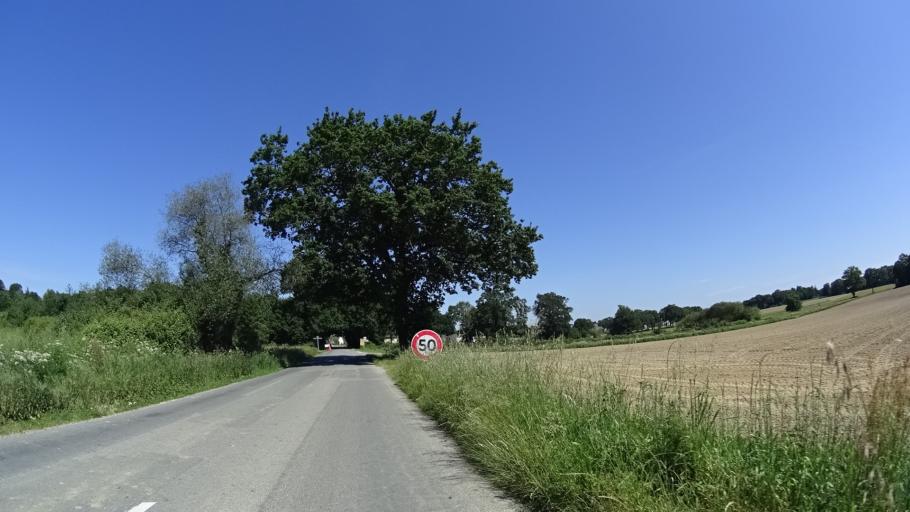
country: FR
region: Brittany
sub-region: Departement d'Ille-et-Vilaine
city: Messac
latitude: 47.8170
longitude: -1.8070
